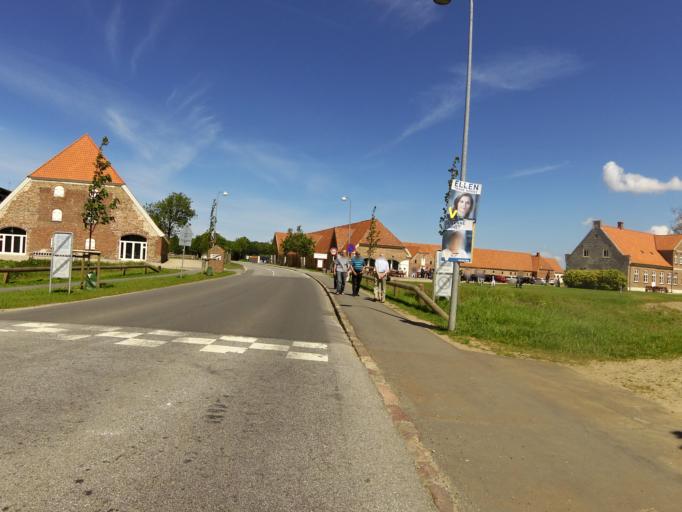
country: DK
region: South Denmark
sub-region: Haderslev Kommune
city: Gram
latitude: 55.2961
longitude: 9.0581
